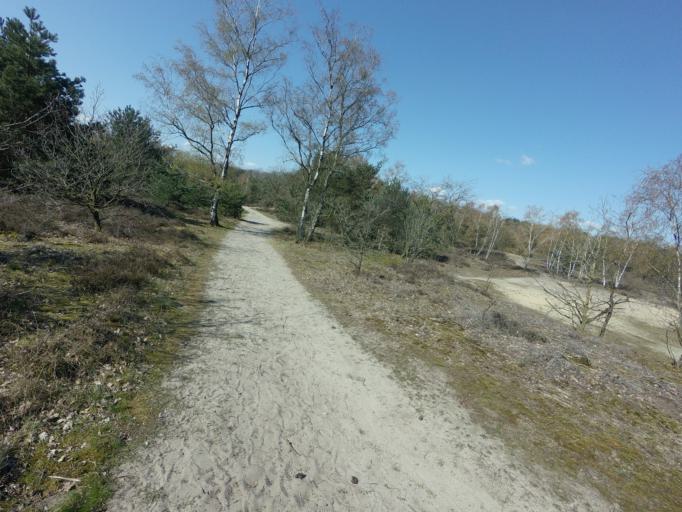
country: NL
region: Limburg
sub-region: Gemeente Bergen
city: Wellerlooi
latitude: 51.6069
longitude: 6.0632
